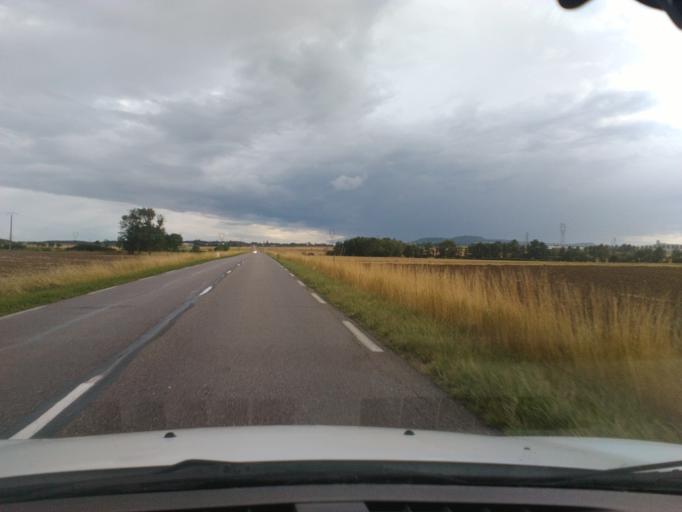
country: FR
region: Lorraine
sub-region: Departement de Meurthe-et-Moselle
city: Pulligny
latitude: 48.4944
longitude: 6.1469
